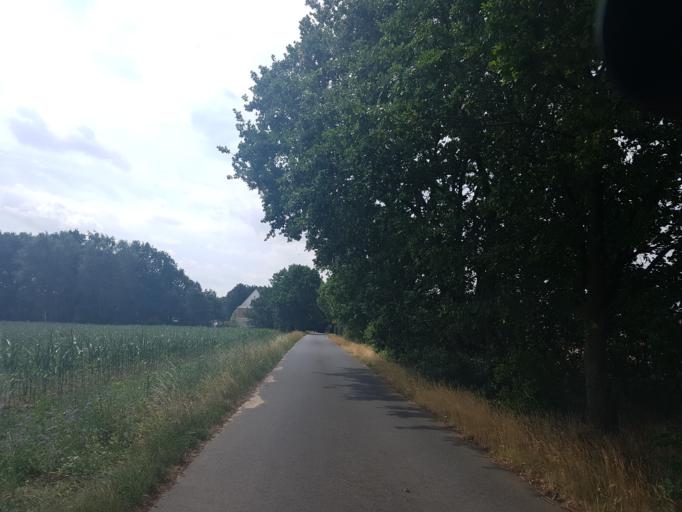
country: DE
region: Brandenburg
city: Treuenbrietzen
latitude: 52.0399
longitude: 12.8107
